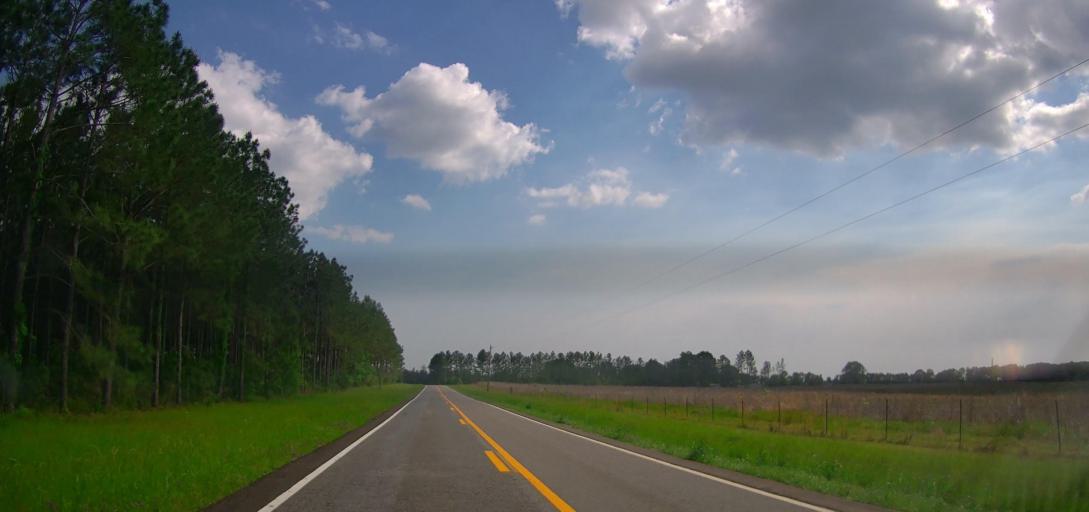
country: US
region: Georgia
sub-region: Laurens County
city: East Dublin
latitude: 32.6397
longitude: -82.8949
